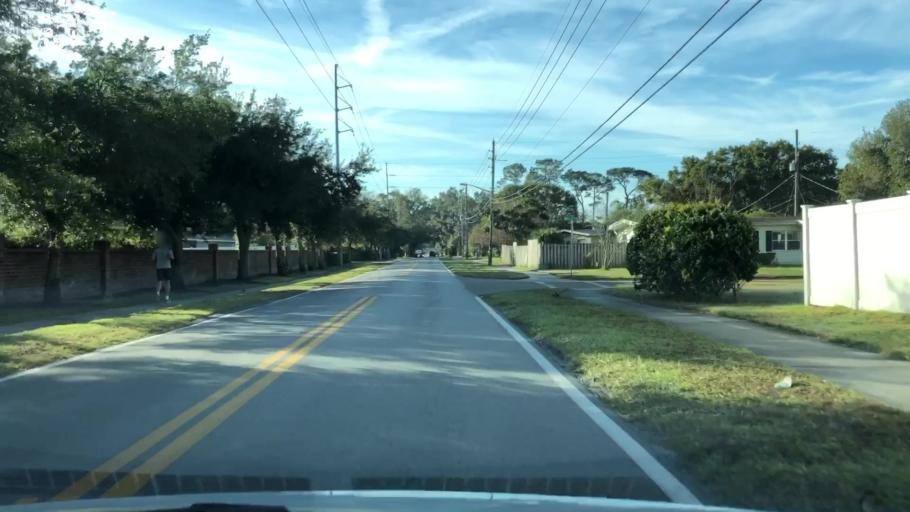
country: US
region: Florida
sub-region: Orange County
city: Conway
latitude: 28.5114
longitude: -81.3392
